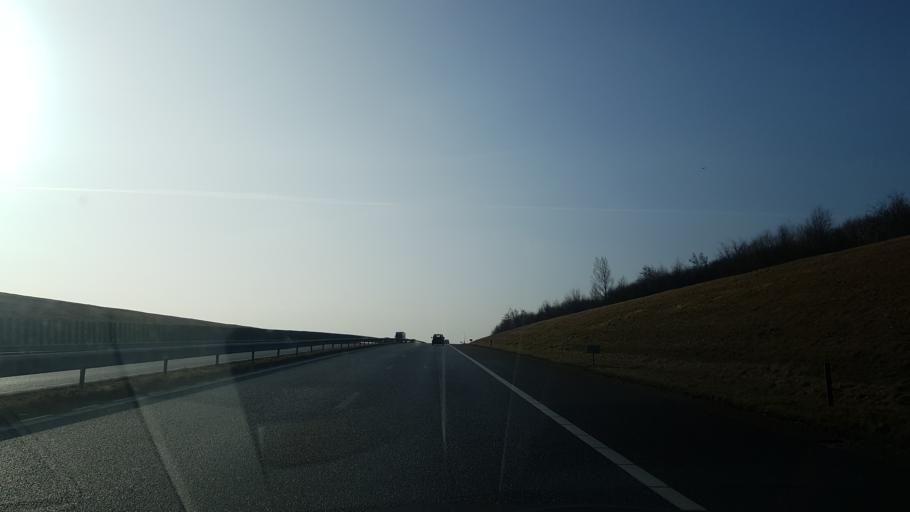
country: NL
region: Friesland
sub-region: Gemeente Boarnsterhim
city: Grou
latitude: 53.0787
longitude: 5.8292
